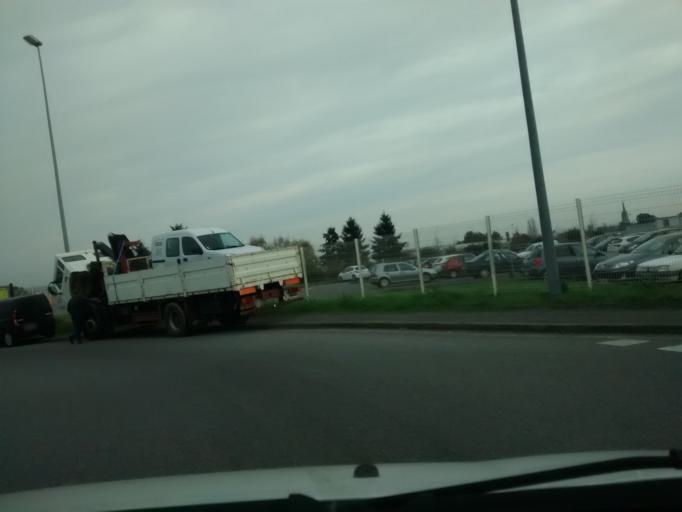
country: FR
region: Brittany
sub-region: Departement d'Ille-et-Vilaine
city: Noyal-sur-Vilaine
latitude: 48.1092
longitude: -1.5334
